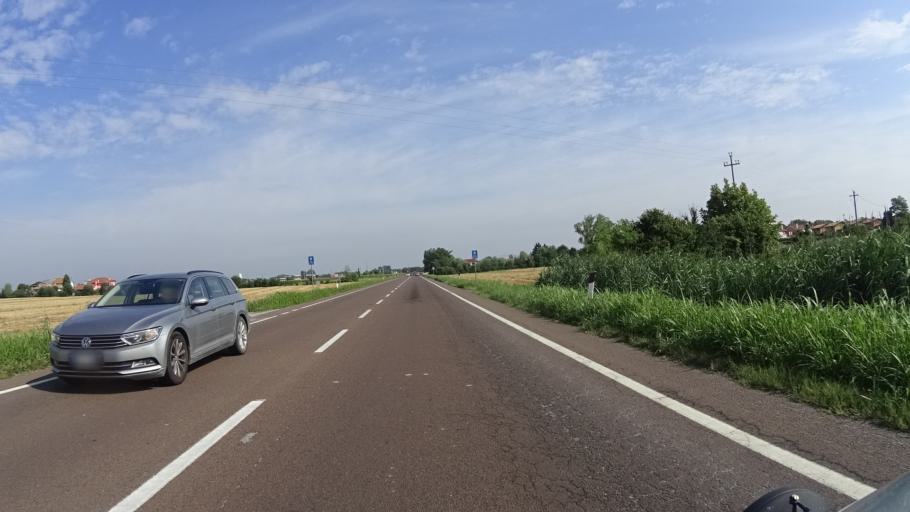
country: IT
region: Veneto
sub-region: Provincia di Venezia
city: San Michele al Tagliamento
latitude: 45.7579
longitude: 12.9870
